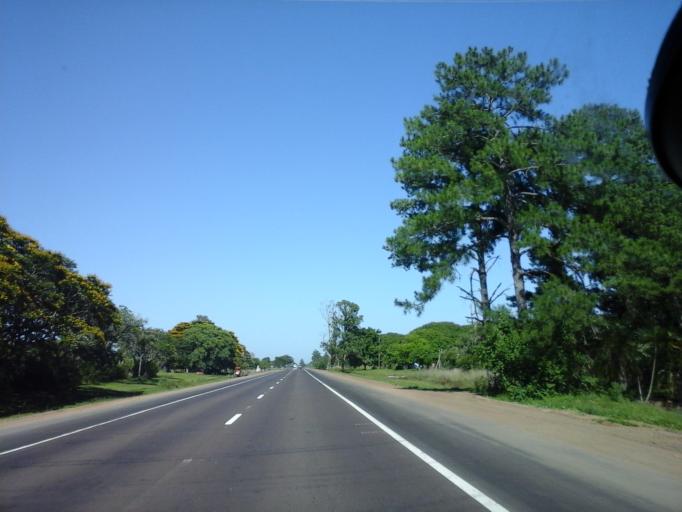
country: AR
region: Corrientes
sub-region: Departamento de Itati
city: Itati
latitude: -27.3669
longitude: -58.3439
